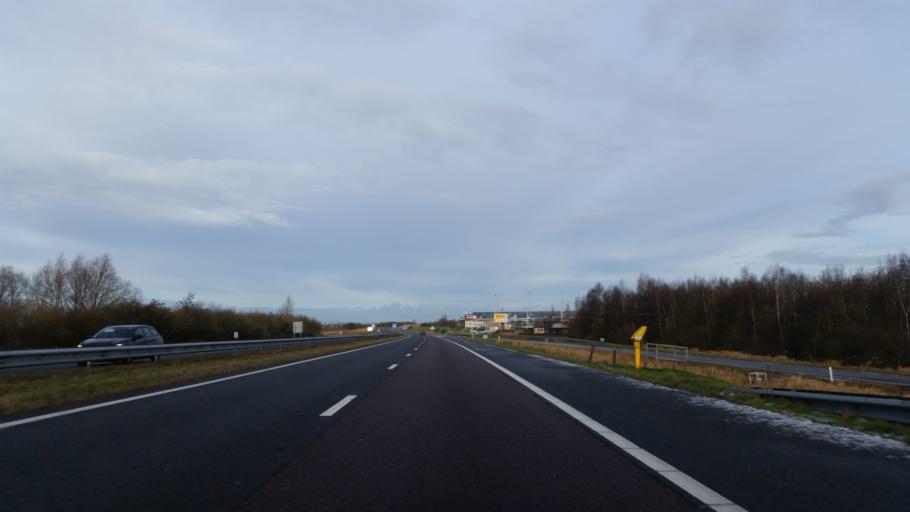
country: NL
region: Friesland
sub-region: Gemeente Boarnsterhim
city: Grou
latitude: 53.0921
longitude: 5.8229
